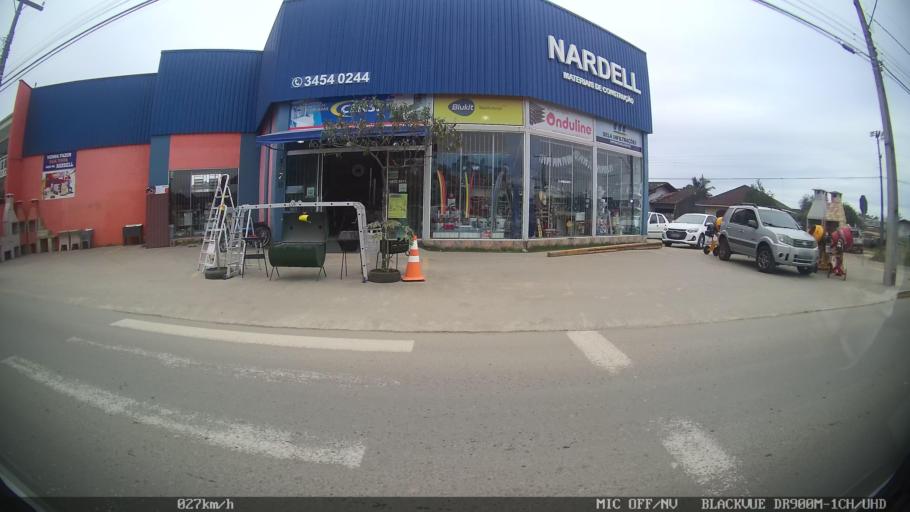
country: BR
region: Santa Catarina
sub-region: Joinville
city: Joinville
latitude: -26.3268
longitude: -48.9079
